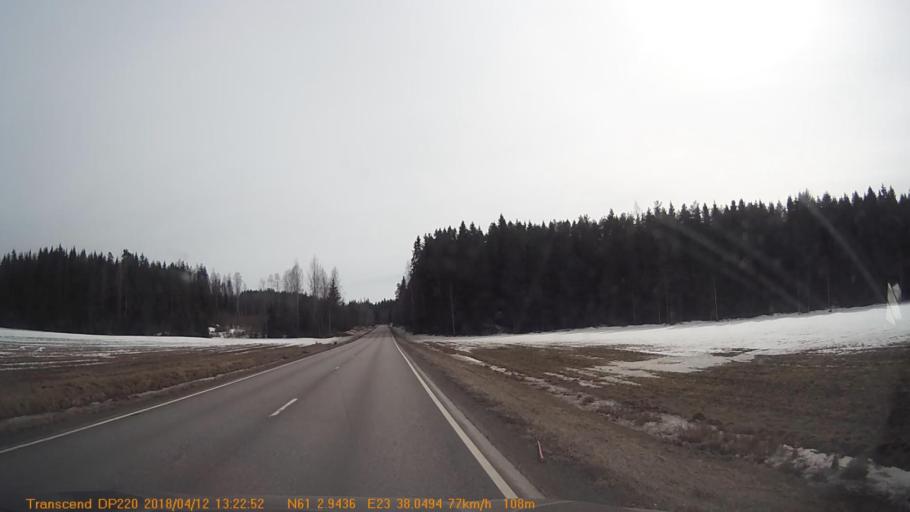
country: FI
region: Pirkanmaa
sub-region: Etelae-Pirkanmaa
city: Urjala
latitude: 61.0481
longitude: 23.6351
